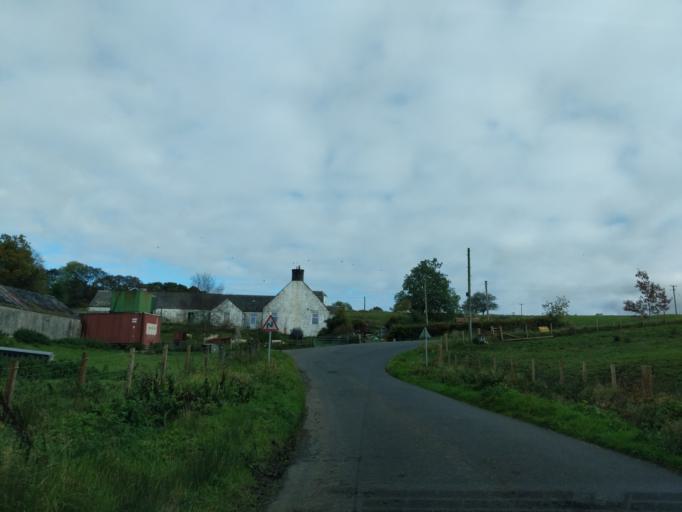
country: GB
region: Scotland
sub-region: Dumfries and Galloway
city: Castle Douglas
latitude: 55.1068
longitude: -4.1230
